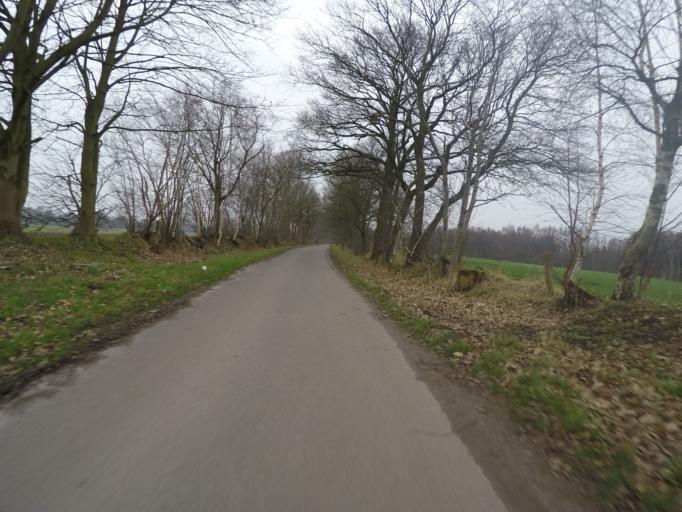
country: DE
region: Schleswig-Holstein
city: Borstel-Hohenraden
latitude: 53.6777
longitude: 9.8191
